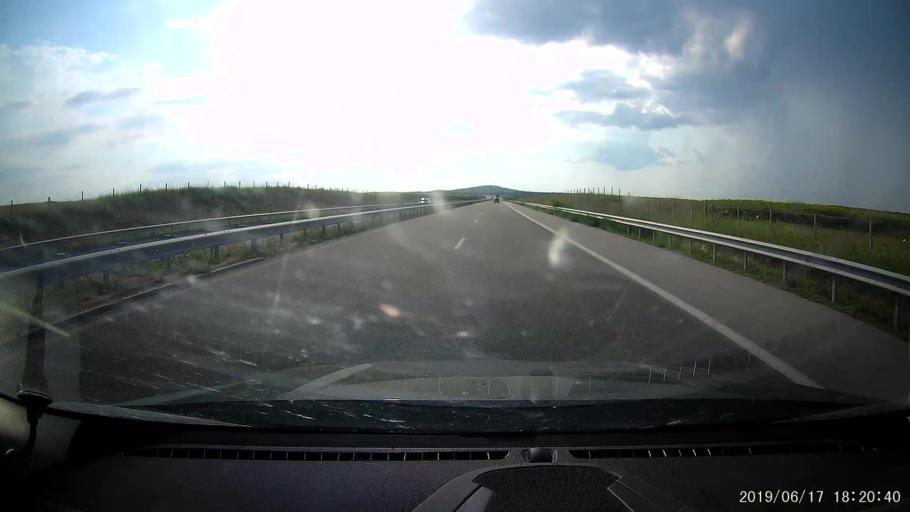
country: BG
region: Khaskovo
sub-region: Obshtina Simeonovgrad
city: Simeonovgrad
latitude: 41.9632
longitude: 25.8060
